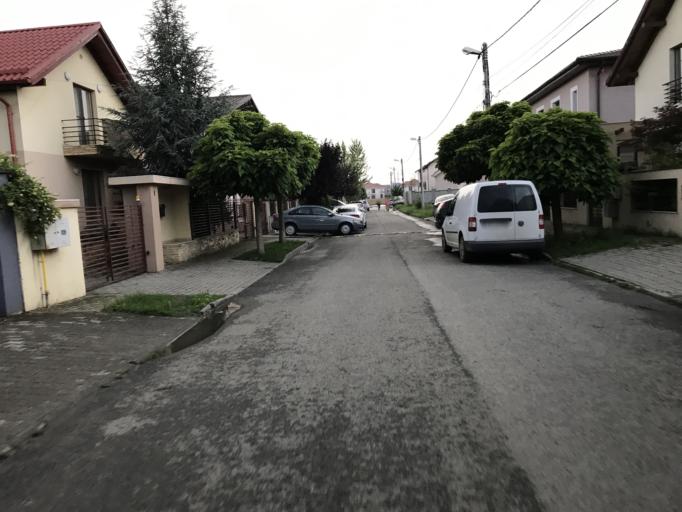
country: RO
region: Timis
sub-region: Comuna Dumbravita
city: Dumbravita
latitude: 45.7889
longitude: 21.2327
